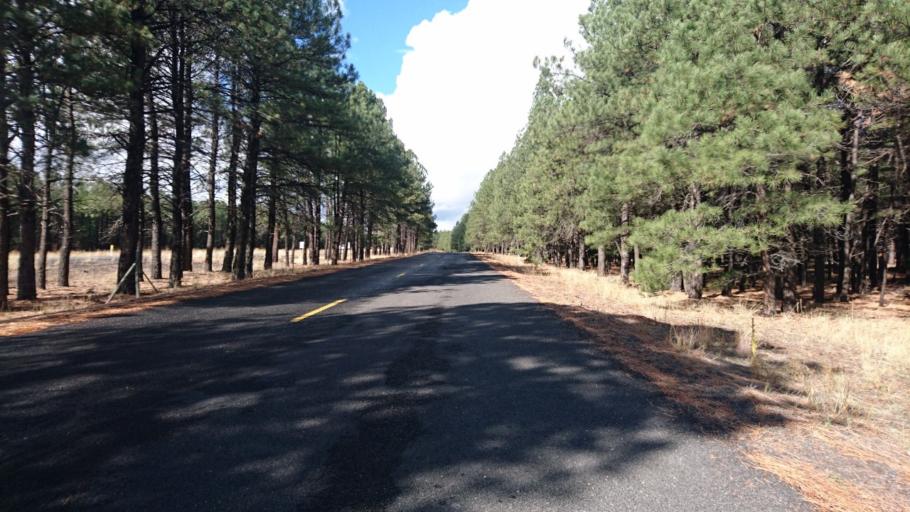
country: US
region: Arizona
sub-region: Coconino County
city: Parks
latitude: 35.2478
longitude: -111.8473
